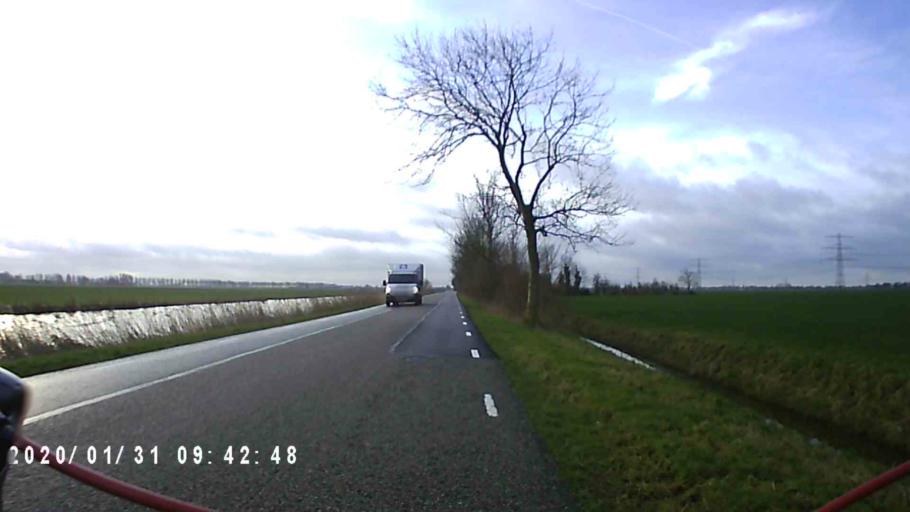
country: NL
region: Groningen
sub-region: Gemeente Zuidhorn
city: Aduard
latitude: 53.2777
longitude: 6.4845
